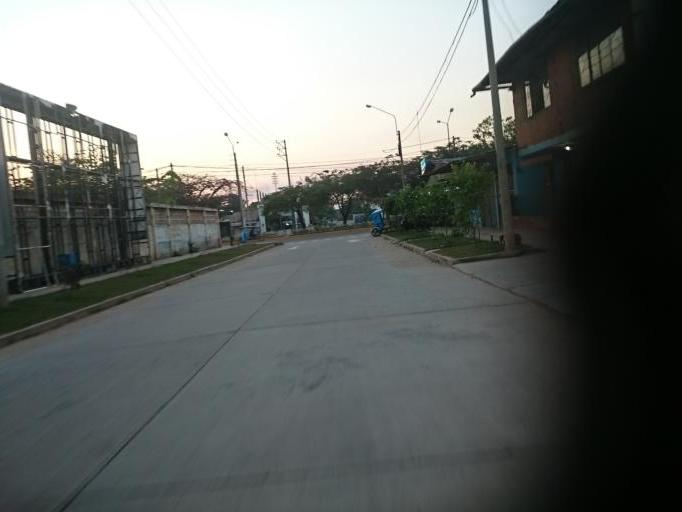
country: PE
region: Ucayali
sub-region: Provincia de Coronel Portillo
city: Pucallpa
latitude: -8.3806
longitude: -74.5369
